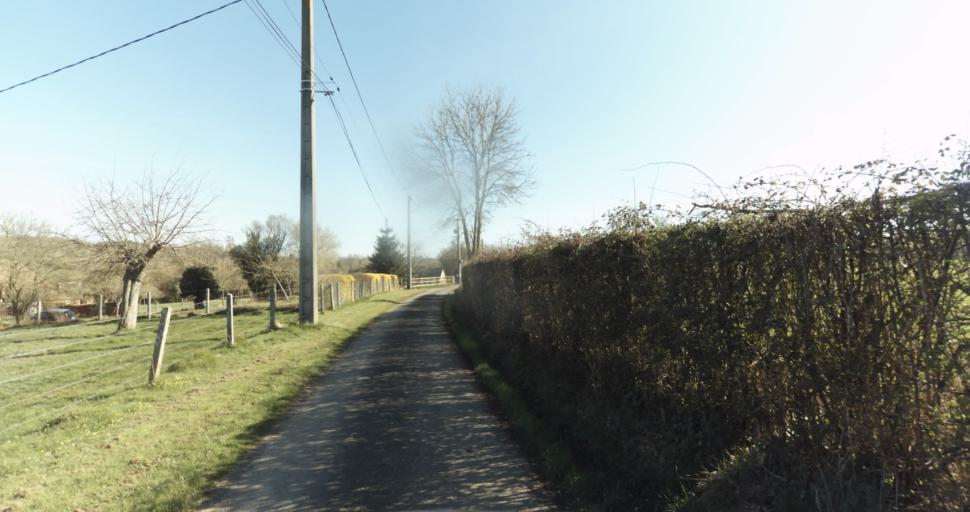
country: FR
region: Lower Normandy
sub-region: Departement du Calvados
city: Livarot
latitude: 49.0226
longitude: 0.0673
